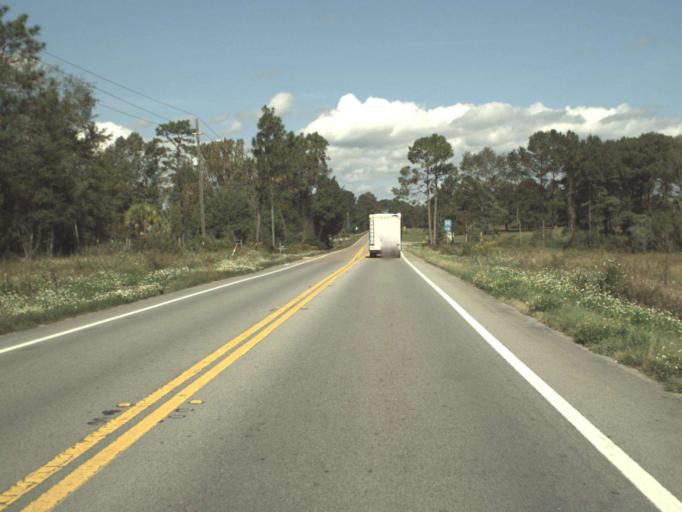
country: US
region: Florida
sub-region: Walton County
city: DeFuniak Springs
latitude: 30.6567
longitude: -86.1178
